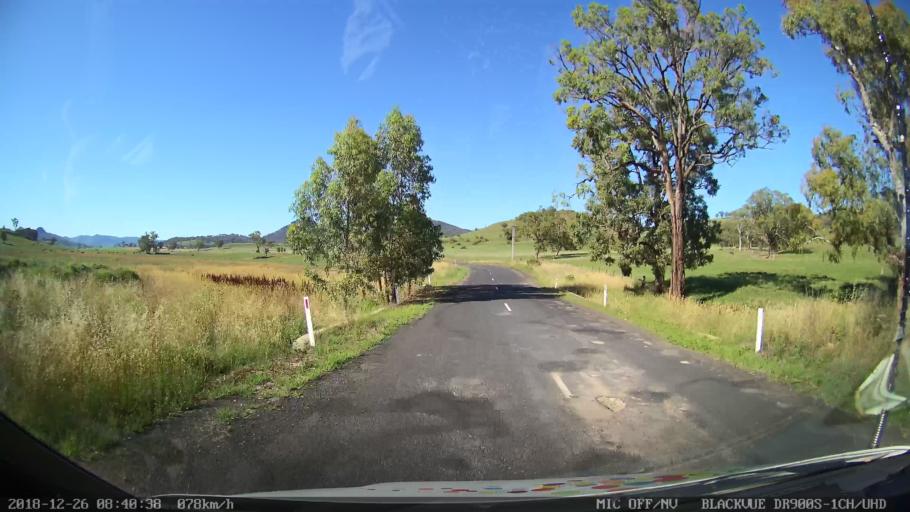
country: AU
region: New South Wales
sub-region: Mid-Western Regional
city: Kandos
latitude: -32.4691
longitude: 150.0752
